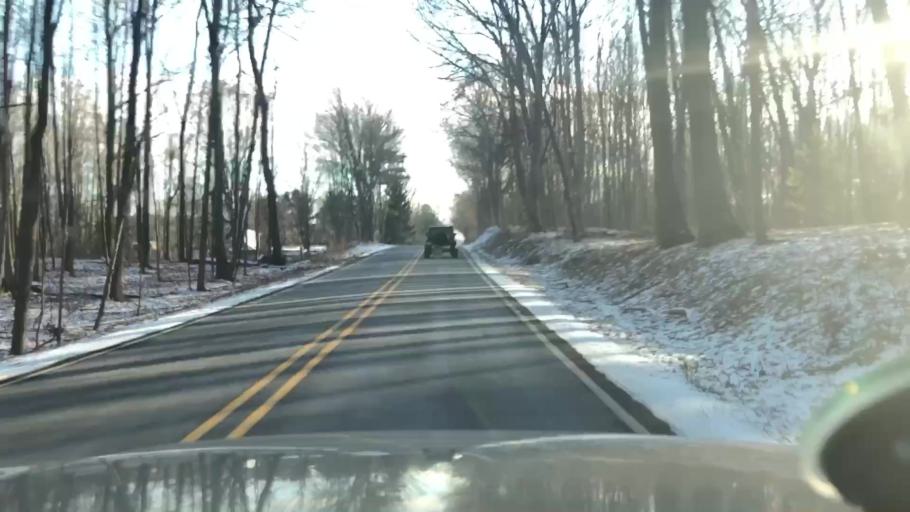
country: US
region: Michigan
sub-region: Jackson County
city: Vandercook Lake
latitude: 42.1097
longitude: -84.4513
